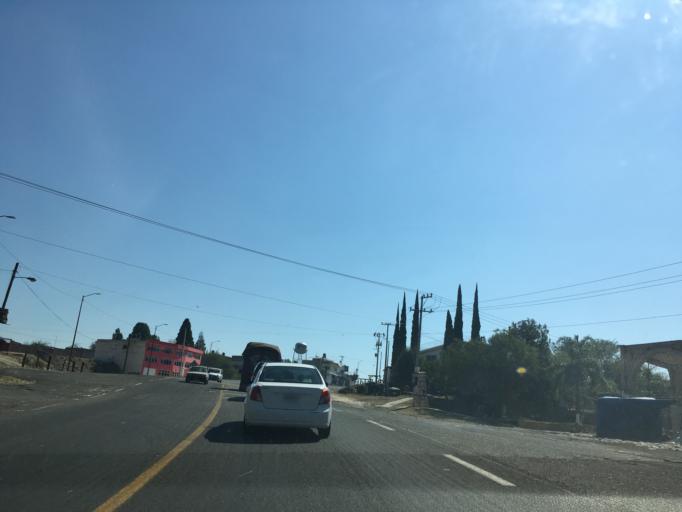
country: MX
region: Michoacan
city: Indaparapeo
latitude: 19.7901
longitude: -100.9751
